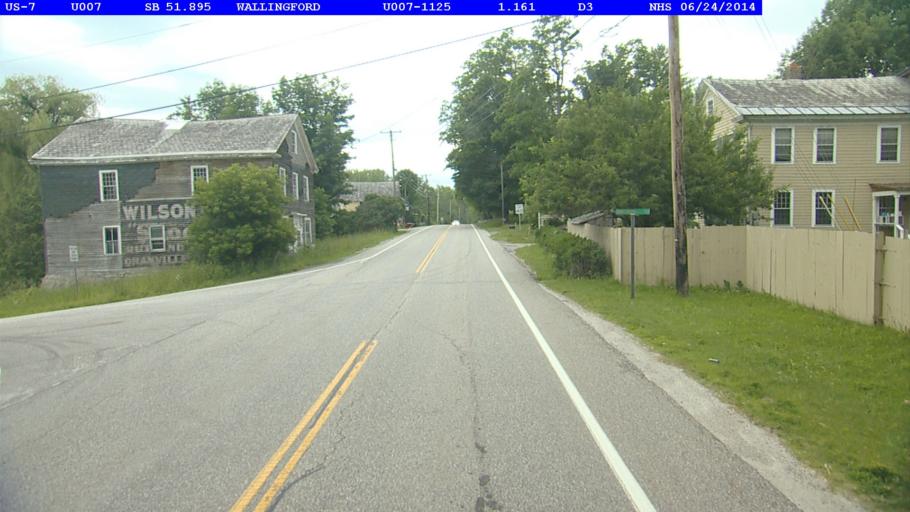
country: US
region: Vermont
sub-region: Rutland County
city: West Rutland
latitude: 43.4133
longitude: -72.9923
